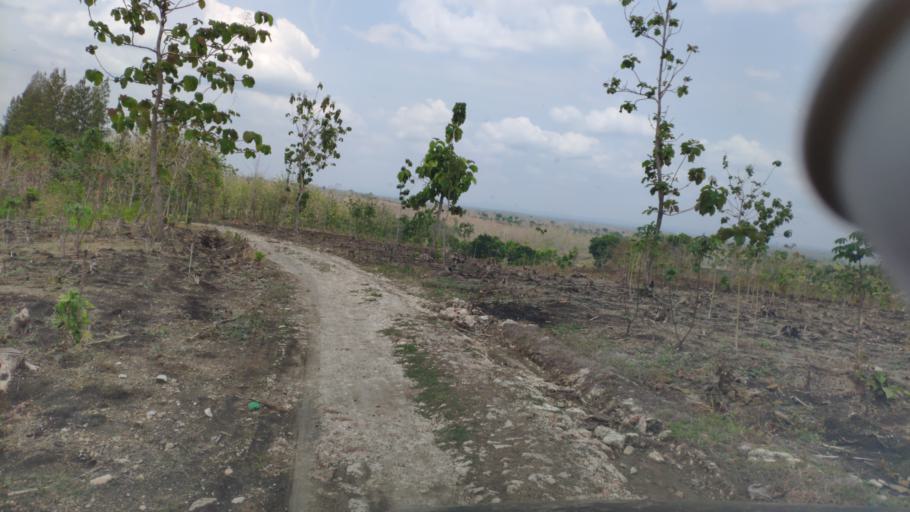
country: ID
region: Central Java
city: Gumiring
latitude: -7.0501
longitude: 111.3982
